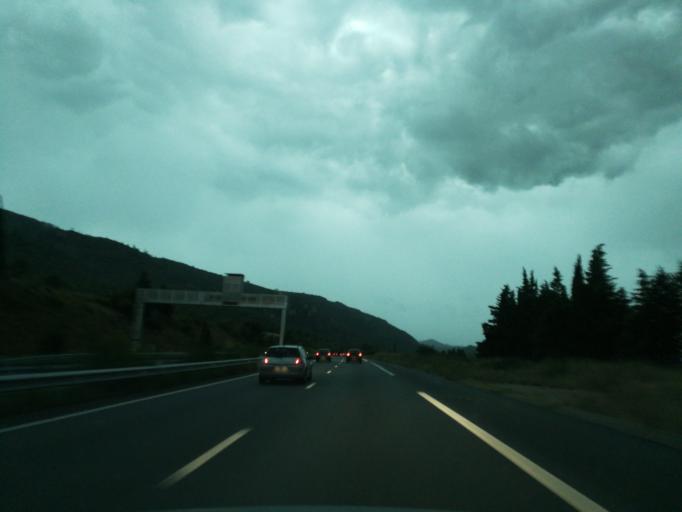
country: FR
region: Languedoc-Roussillon
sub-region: Departement de l'Aude
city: Capendu
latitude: 43.1808
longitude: 2.5093
